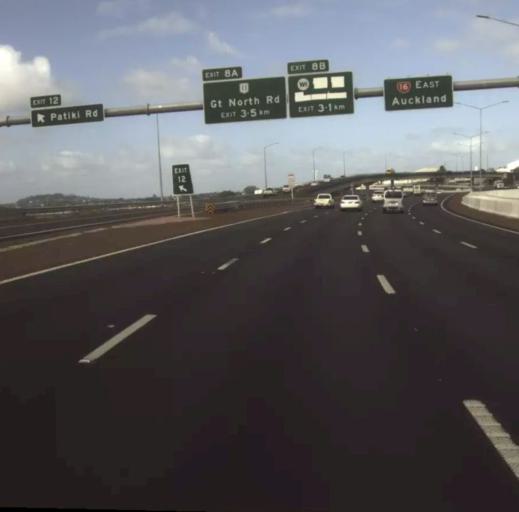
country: NZ
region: Auckland
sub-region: Auckland
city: Rosebank
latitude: -36.8624
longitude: 174.6640
